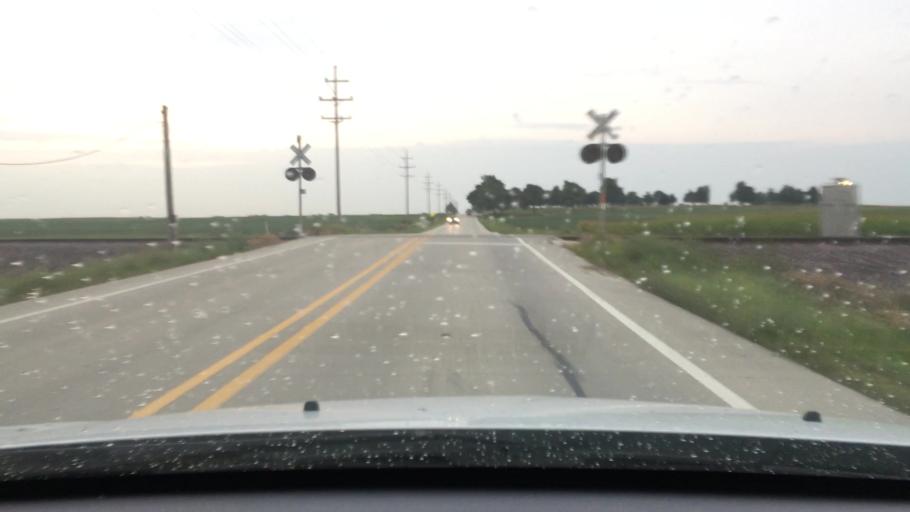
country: US
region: Illinois
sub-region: DeKalb County
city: Waterman
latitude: 41.8493
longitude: -88.7844
